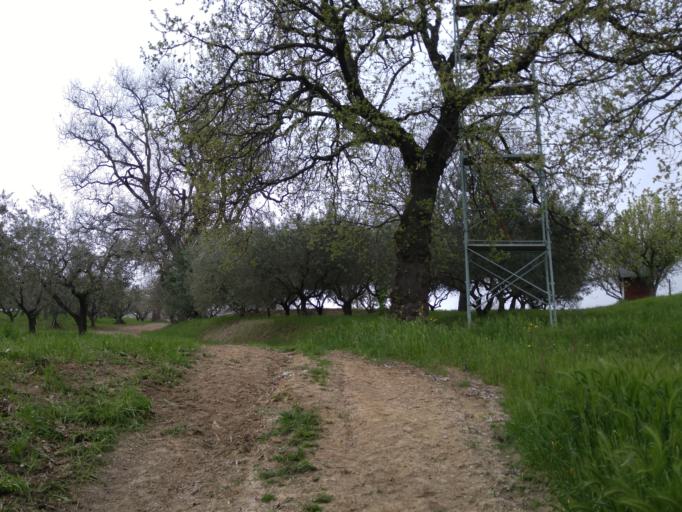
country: IT
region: The Marches
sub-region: Provincia di Pesaro e Urbino
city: Calcinelli
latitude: 43.7653
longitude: 12.9091
